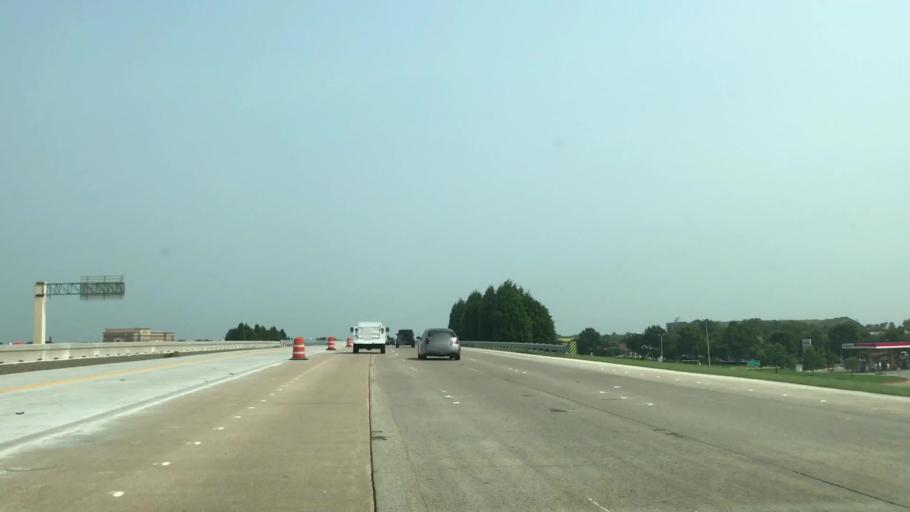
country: US
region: Texas
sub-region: Dallas County
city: Sachse
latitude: 32.9671
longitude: -96.6439
